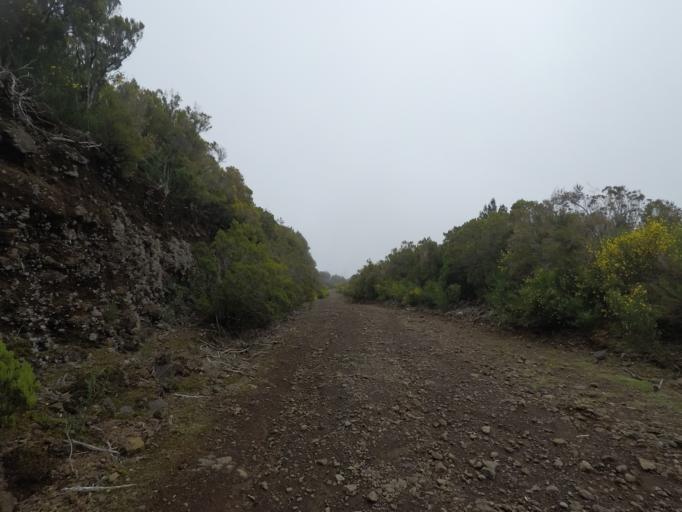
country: PT
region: Madeira
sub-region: Sao Vicente
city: Sao Vicente
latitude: 32.7736
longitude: -17.0658
